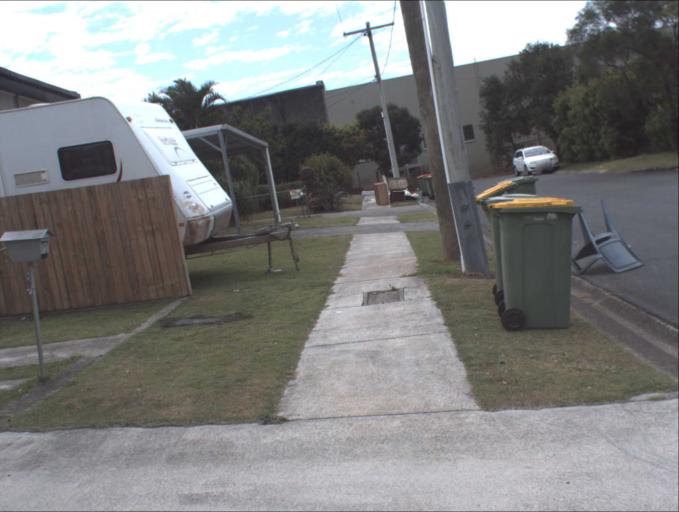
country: AU
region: Queensland
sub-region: Logan
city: Logan City
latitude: -27.6268
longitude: 153.1199
